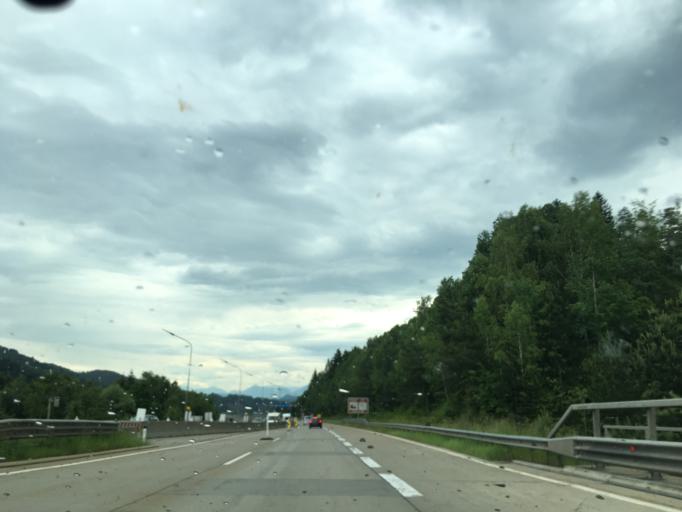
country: AT
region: Carinthia
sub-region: Villach Stadt
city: Villach
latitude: 46.6428
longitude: 13.7981
